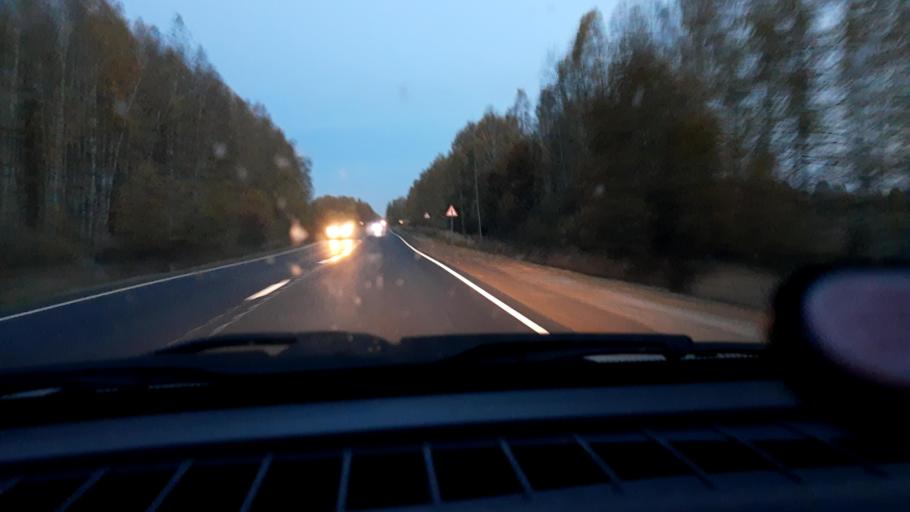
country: RU
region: Nizjnij Novgorod
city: Novaya Balakhna
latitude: 56.5712
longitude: 43.7091
